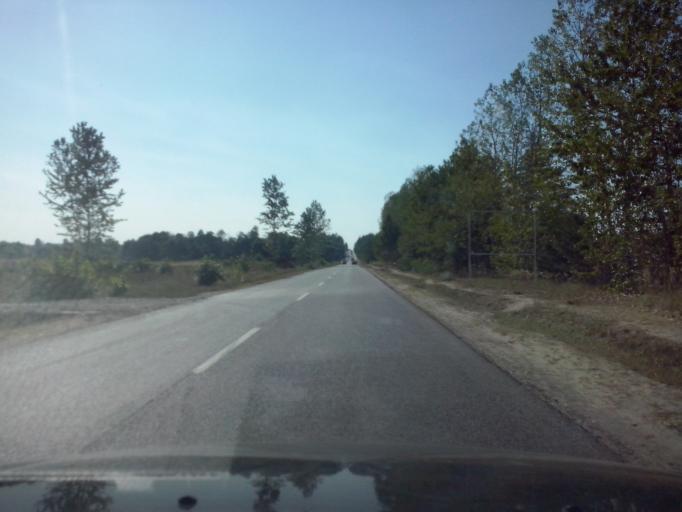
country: PL
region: Swietokrzyskie
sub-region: Powiat kielecki
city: Domaszowice
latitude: 50.8140
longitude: 20.7067
